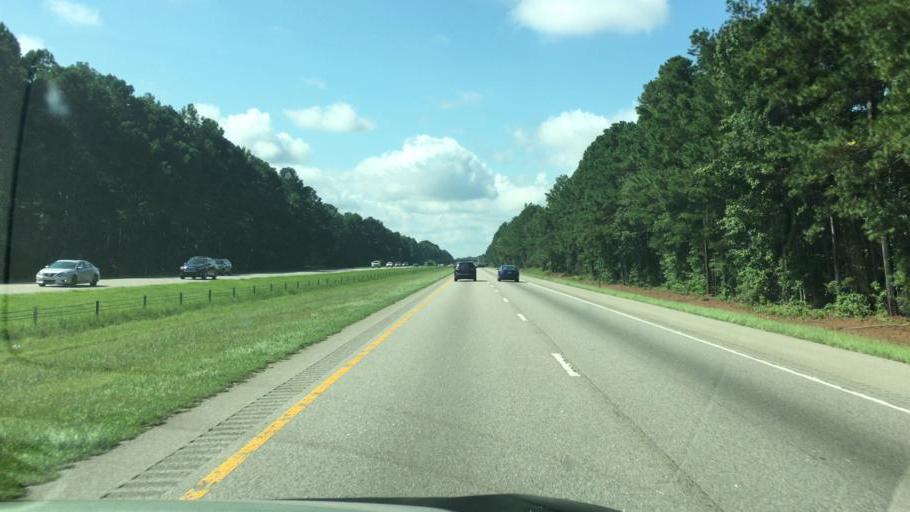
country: US
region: North Carolina
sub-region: Robeson County
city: Saint Pauls
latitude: 34.7787
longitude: -78.9957
